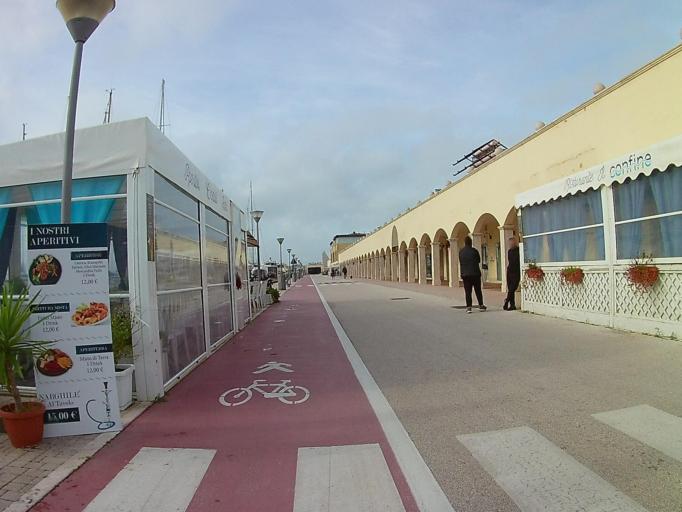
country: IT
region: Latium
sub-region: Citta metropolitana di Roma Capitale
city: Fiumicino-Isola Sacra
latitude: 41.7392
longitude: 12.2446
